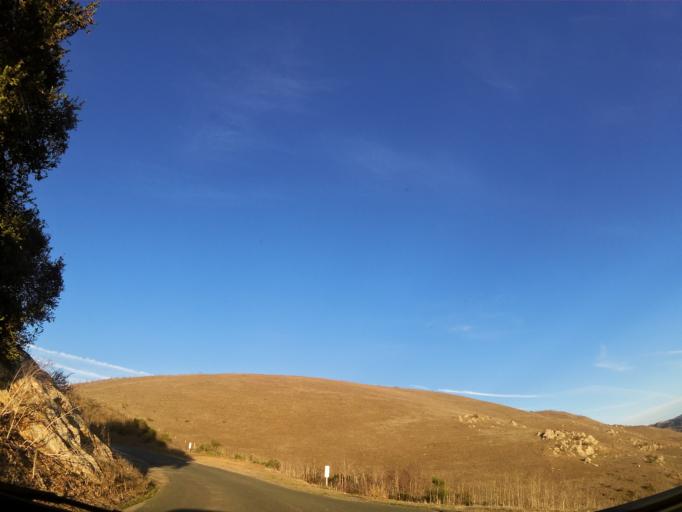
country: US
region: California
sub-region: San Benito County
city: San Juan Bautista
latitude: 36.8125
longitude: -121.5757
